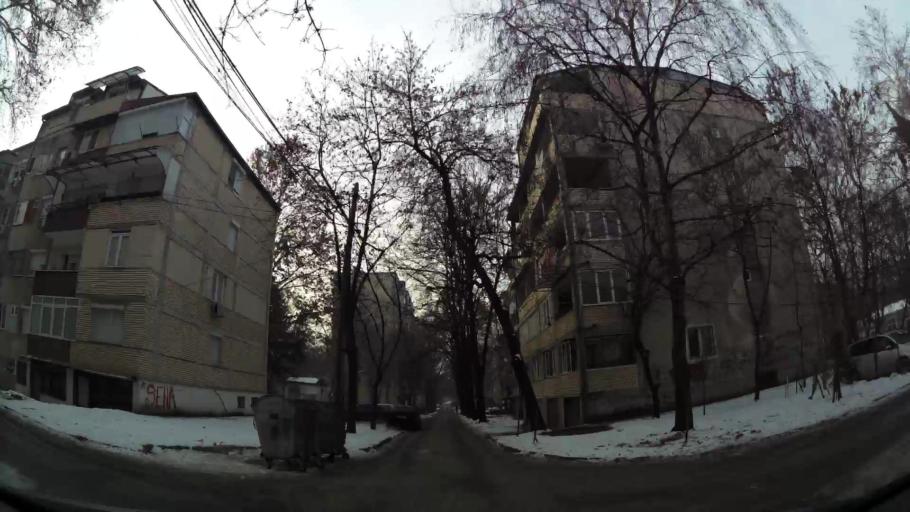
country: MK
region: Cair
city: Cair
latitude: 42.0200
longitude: 21.4423
